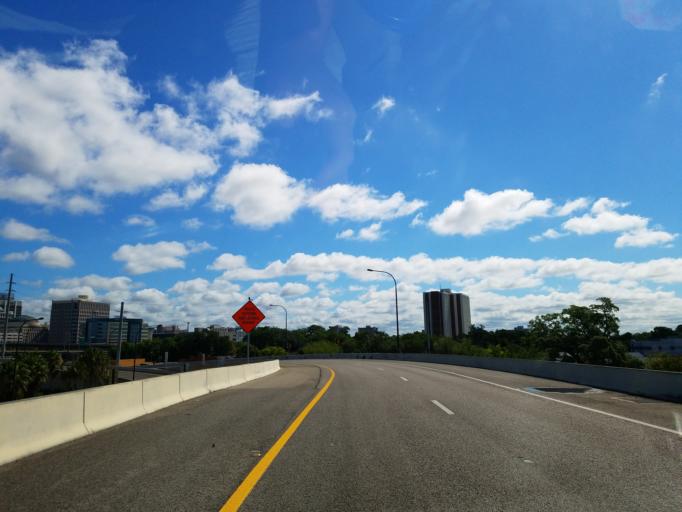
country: US
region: Florida
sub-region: Orange County
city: Orlando
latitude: 28.5319
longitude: -81.3842
